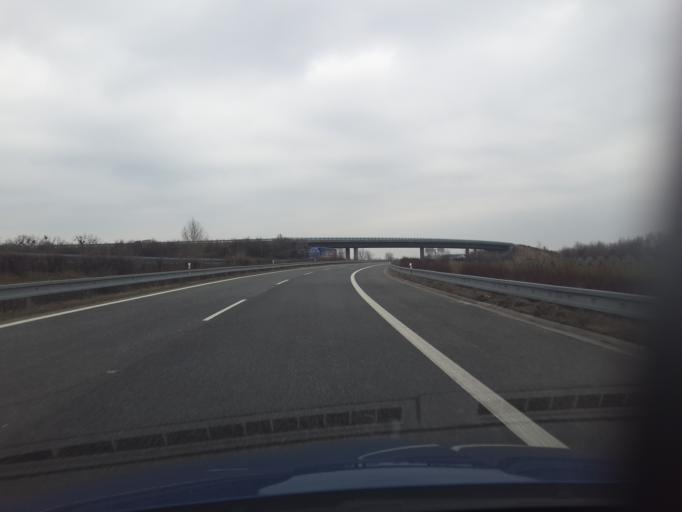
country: AT
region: Burgenland
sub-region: Politischer Bezirk Neusiedl am See
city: Kittsee
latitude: 48.0736
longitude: 17.0992
